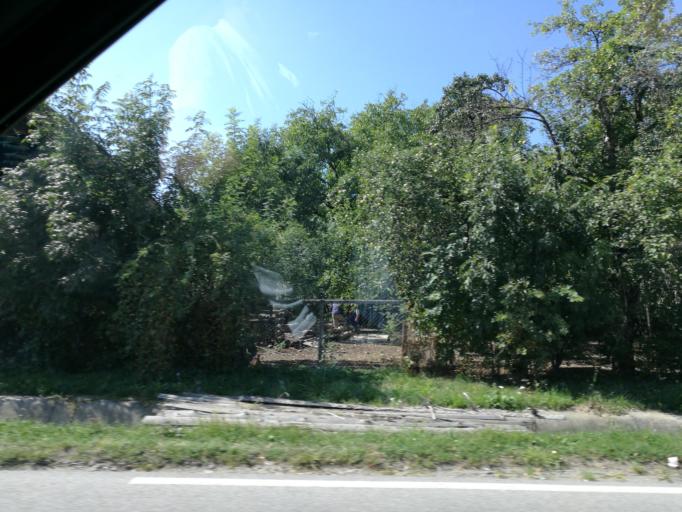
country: RO
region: Suceava
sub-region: Comuna Putna
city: Gura Putnei
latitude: 47.8905
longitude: 25.6106
